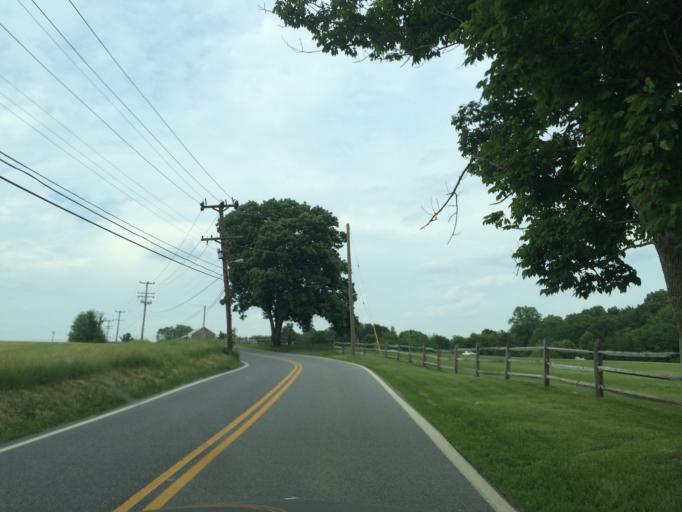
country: US
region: Maryland
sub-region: Baltimore County
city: Randallstown
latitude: 39.3931
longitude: -76.8641
